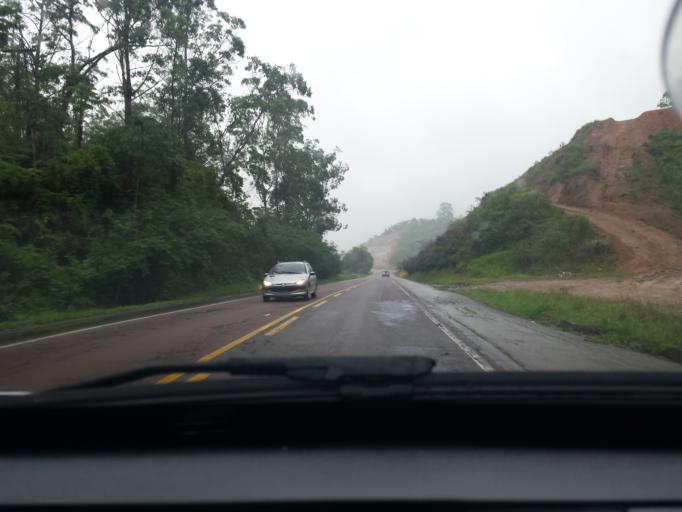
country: BR
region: Santa Catarina
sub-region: Itajai
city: Itajai
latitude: -26.8399
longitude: -48.7835
